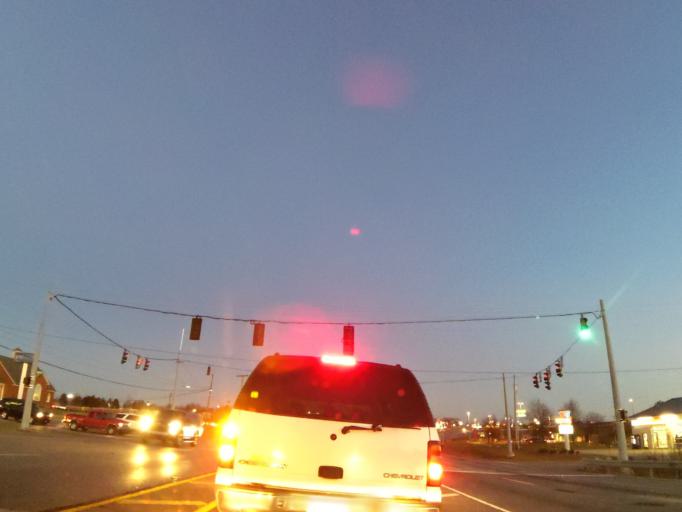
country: US
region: Kentucky
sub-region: Laurel County
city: London
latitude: 37.1113
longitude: -84.0938
